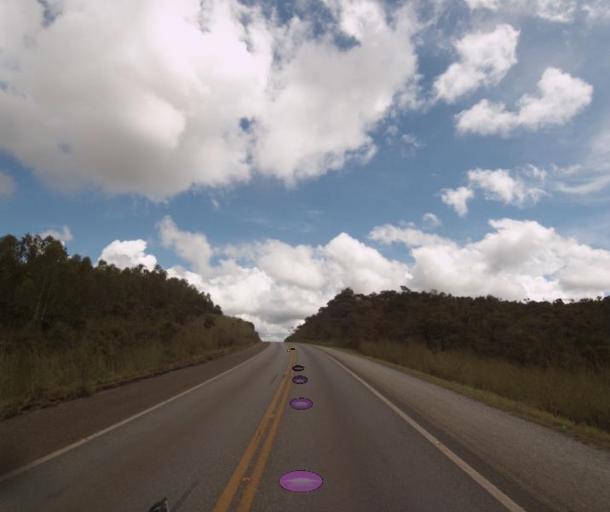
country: BR
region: Goias
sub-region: Pirenopolis
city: Pirenopolis
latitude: -15.7492
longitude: -48.6026
